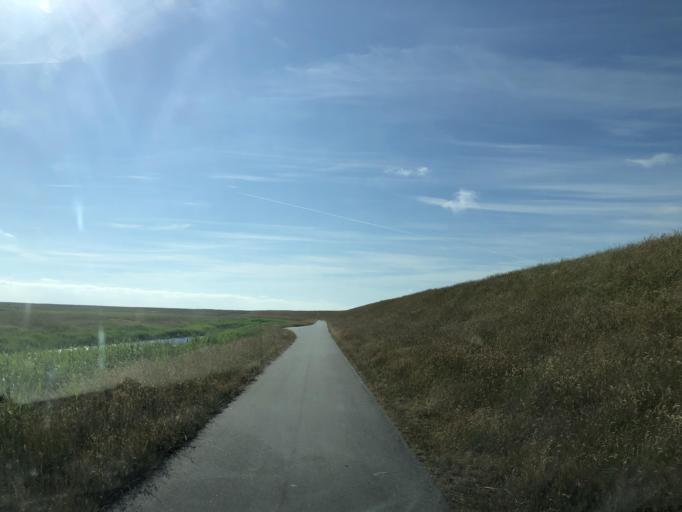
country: DK
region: South Denmark
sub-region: Esbjerg Kommune
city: Tjaereborg
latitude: 55.2930
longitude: 8.5657
